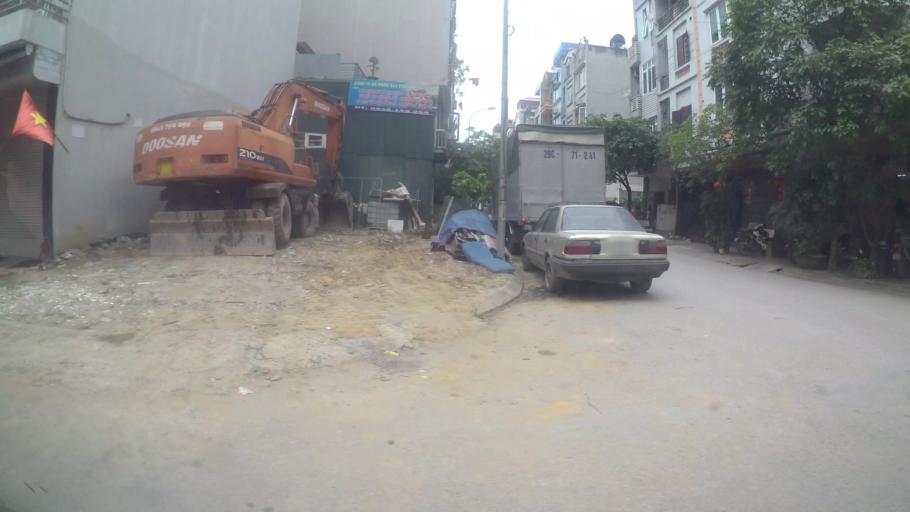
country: VN
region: Ha Noi
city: Ha Dong
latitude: 20.9687
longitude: 105.7668
